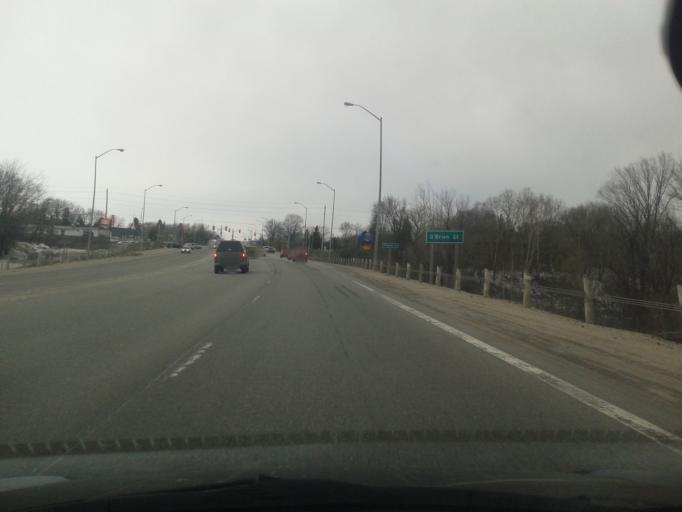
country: CA
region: Ontario
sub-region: Nipissing District
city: North Bay
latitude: 46.3278
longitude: -79.4548
